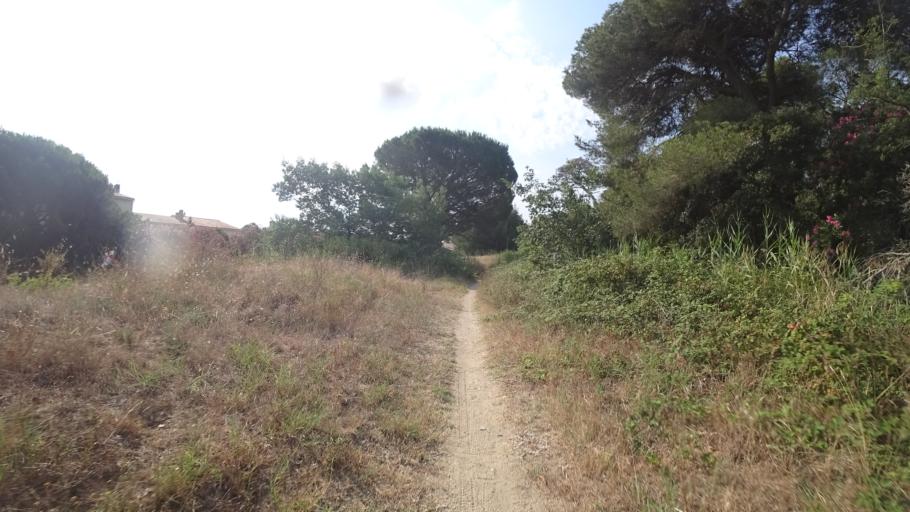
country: FR
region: Languedoc-Roussillon
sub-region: Departement des Pyrenees-Orientales
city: Canet-en-Roussillon
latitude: 42.6887
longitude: 3.0280
